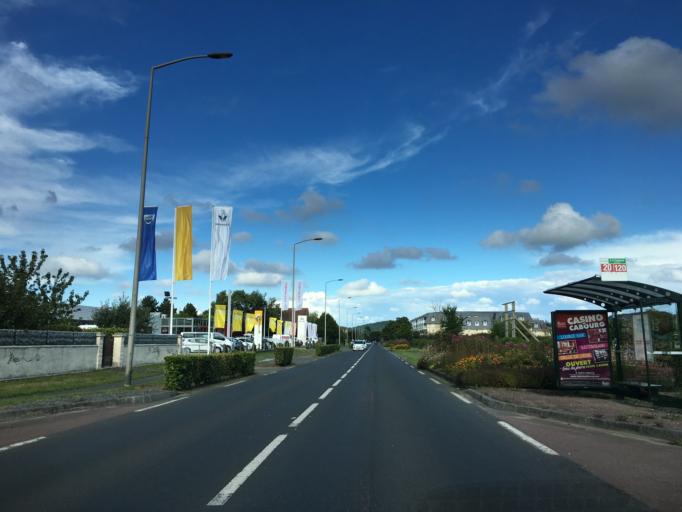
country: FR
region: Lower Normandy
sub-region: Departement du Calvados
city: Cabourg
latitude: 49.2841
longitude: -0.1318
